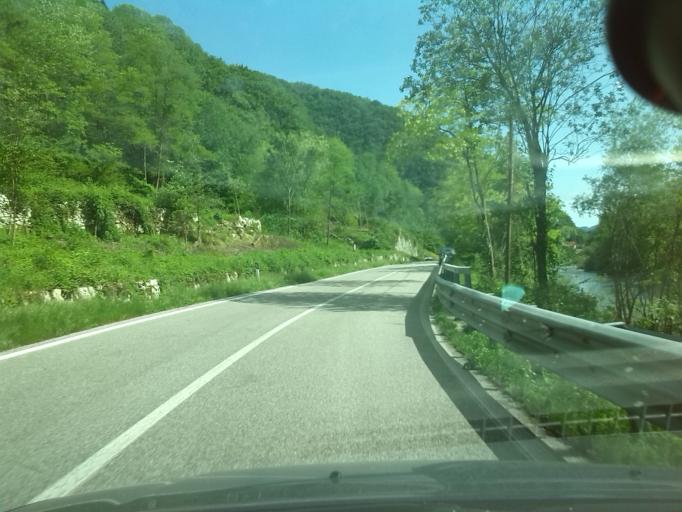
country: IT
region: Friuli Venezia Giulia
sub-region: Provincia di Udine
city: Pulfero
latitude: 46.1859
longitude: 13.4752
